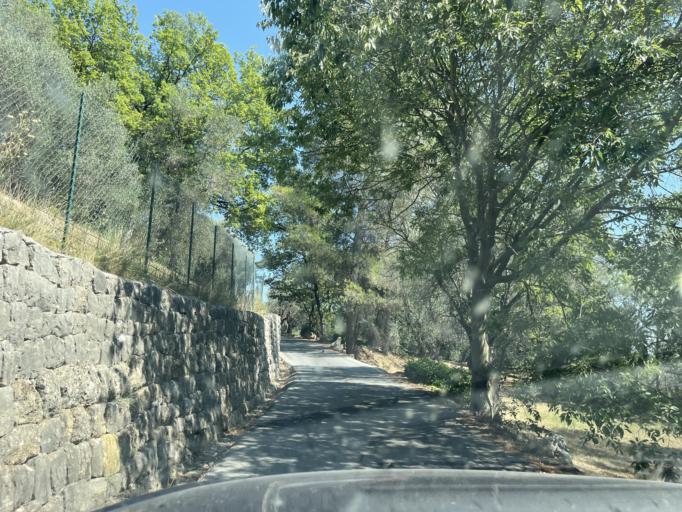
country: FR
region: Provence-Alpes-Cote d'Azur
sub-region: Departement des Alpes-Maritimes
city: Mouans-Sartoux
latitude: 43.6389
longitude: 6.9715
